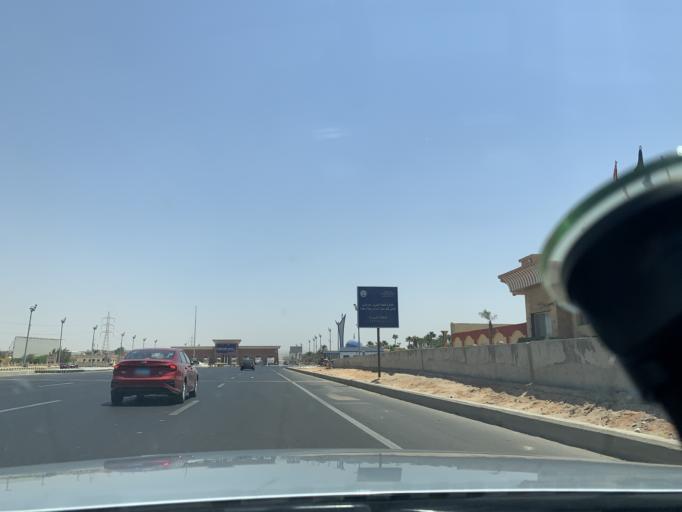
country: EG
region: Muhafazat al Qahirah
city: Halwan
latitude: 29.9643
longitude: 31.4773
